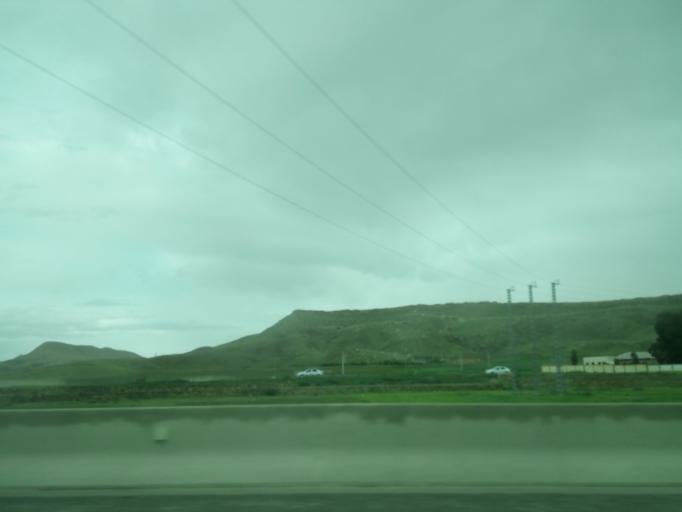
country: DZ
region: Medea
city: Ksar el Boukhari
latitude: 35.8233
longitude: 2.7690
